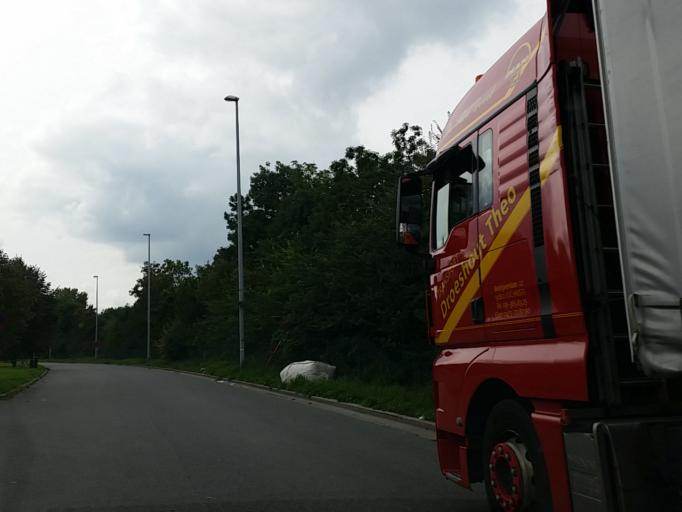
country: BE
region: Flanders
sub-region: Provincie Vlaams-Brabant
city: Steenokkerzeel
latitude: 50.9380
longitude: 4.4748
